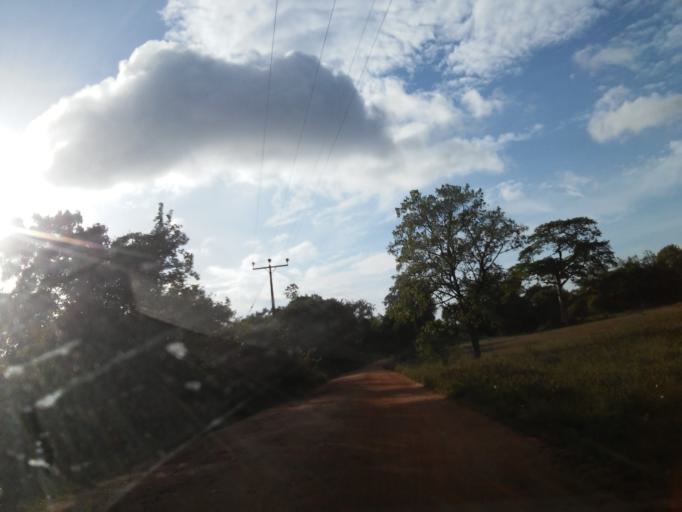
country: LK
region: Central
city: Sigiriya
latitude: 8.1717
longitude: 80.6797
